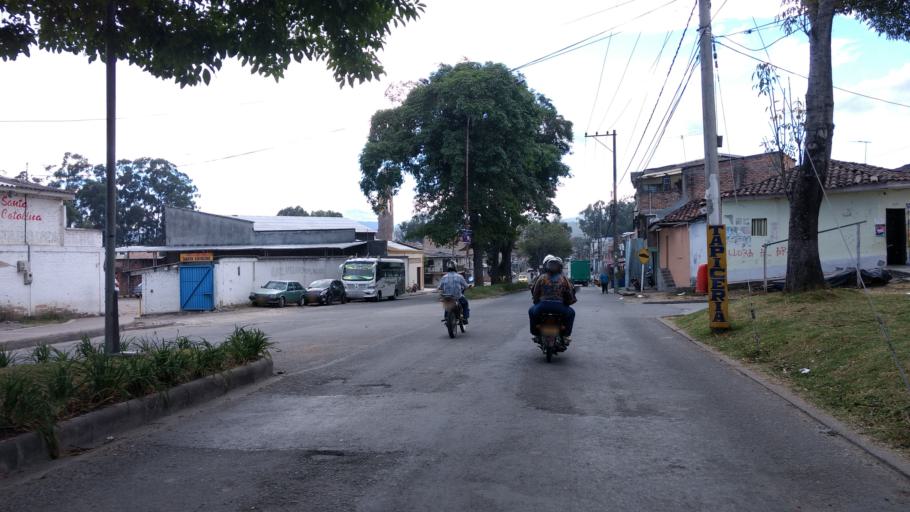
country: CO
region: Cauca
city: Popayan
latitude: 2.4460
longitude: -76.6136
